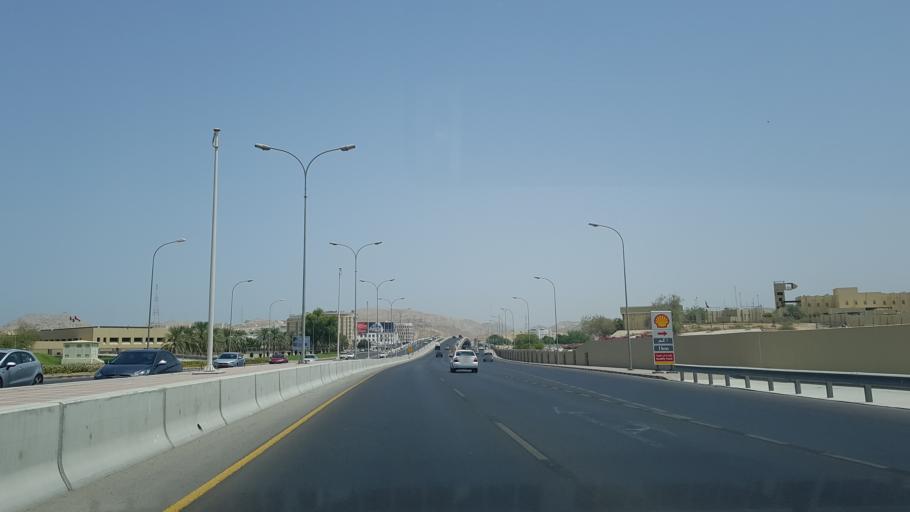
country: OM
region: Muhafazat Masqat
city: Muscat
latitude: 23.6134
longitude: 58.4880
